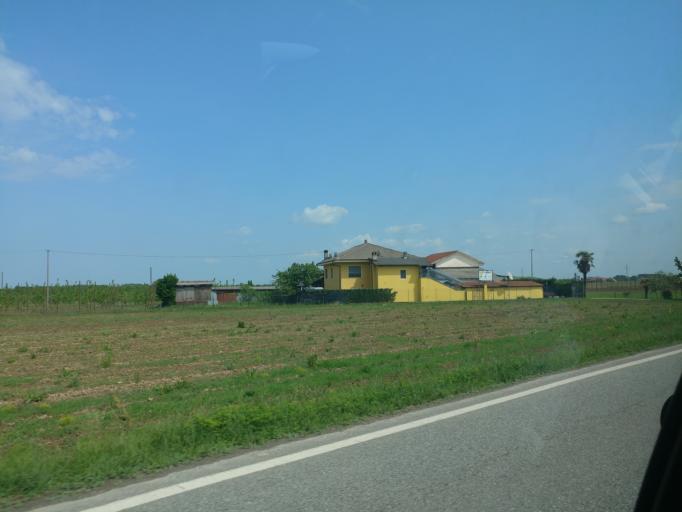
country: IT
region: Piedmont
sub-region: Provincia di Torino
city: Cavour
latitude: 44.7616
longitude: 7.3983
